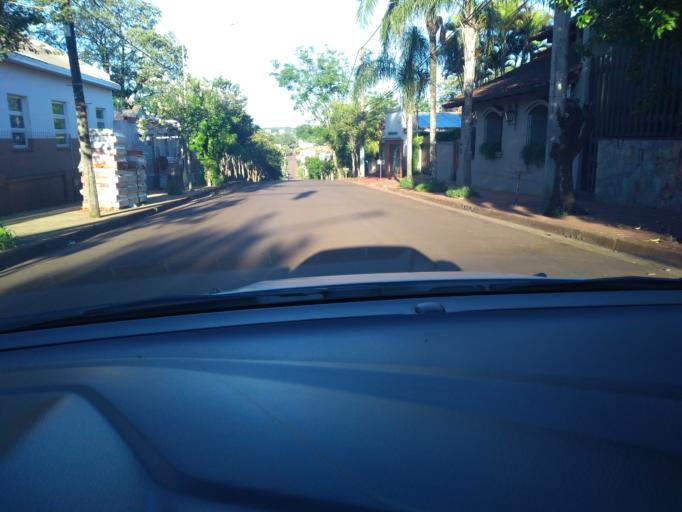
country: AR
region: Misiones
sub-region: Departamento de Obera
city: Obera
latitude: -27.4834
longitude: -55.1196
